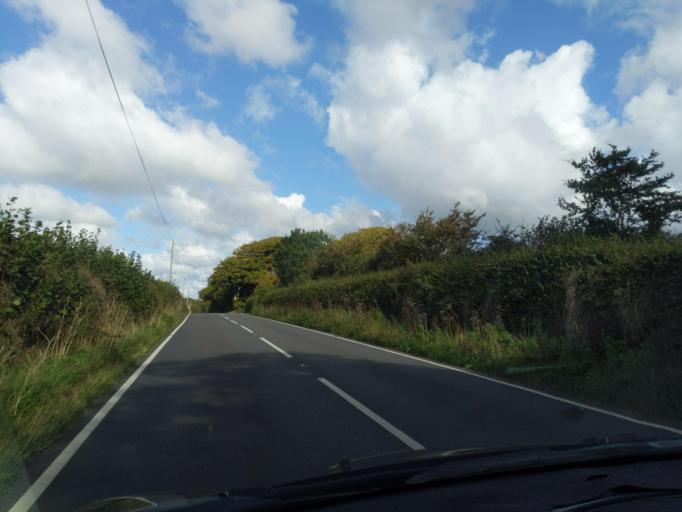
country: GB
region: England
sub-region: Devon
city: Great Torrington
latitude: 50.9084
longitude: -4.2471
